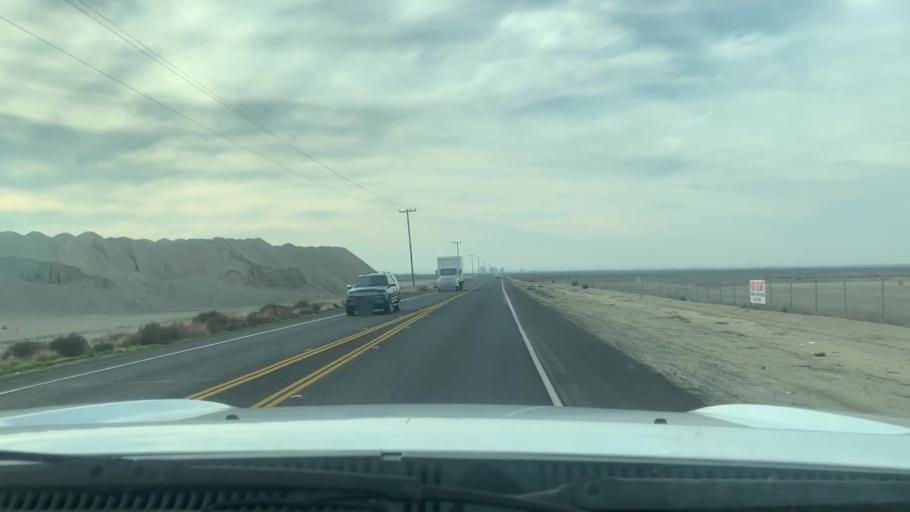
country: US
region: California
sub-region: Kern County
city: Buttonwillow
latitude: 35.4994
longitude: -119.5482
